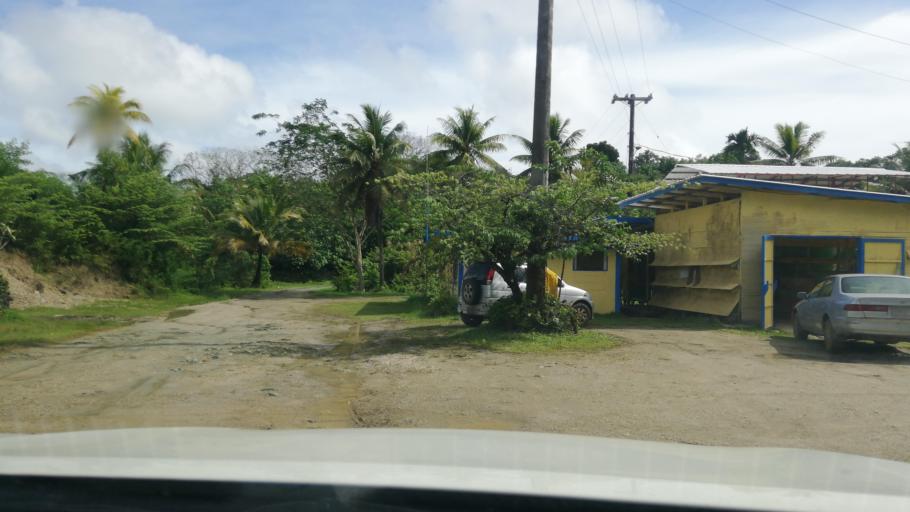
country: FM
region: Yap
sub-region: Weloy Municipality
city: Colonia
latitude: 9.5081
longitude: 138.1012
